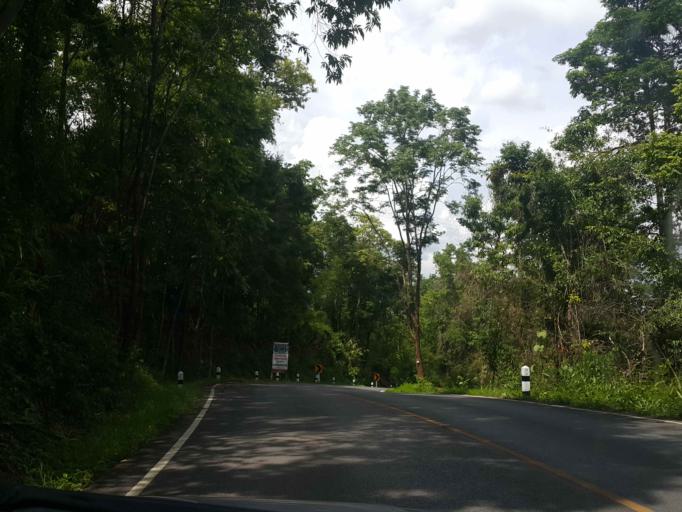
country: TH
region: Nan
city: Ban Luang
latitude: 18.8774
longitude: 100.5405
